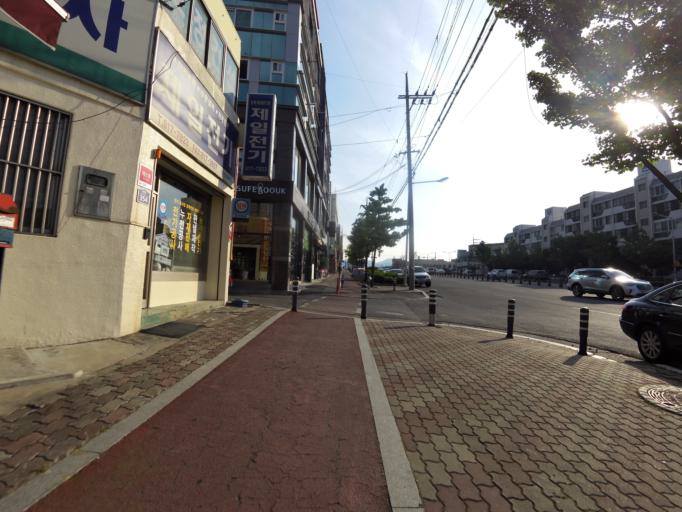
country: KR
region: Gyeongsangbuk-do
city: Gyeongsan-si
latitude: 35.8404
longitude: 128.7596
